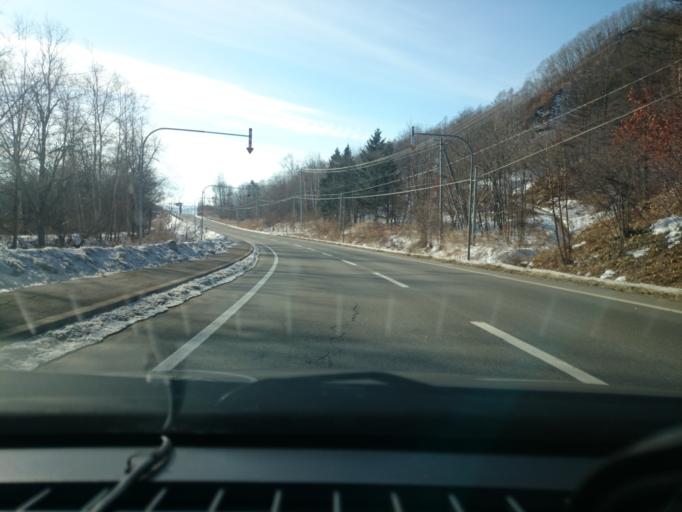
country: JP
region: Hokkaido
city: Otofuke
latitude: 43.2540
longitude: 143.5666
